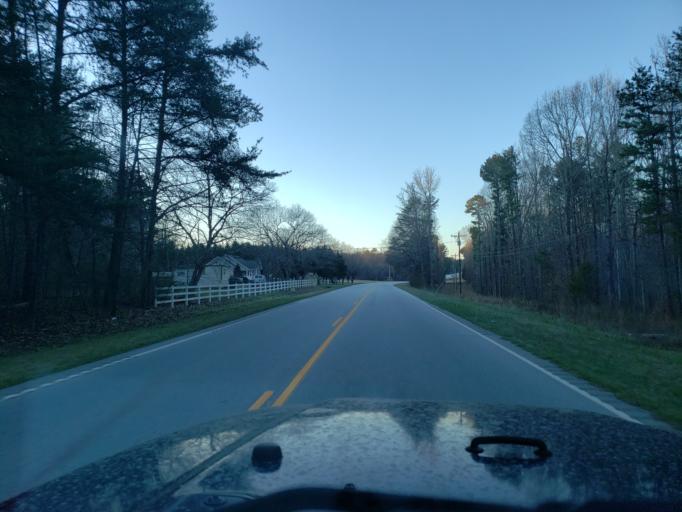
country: US
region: North Carolina
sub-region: Cleveland County
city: Kings Mountain
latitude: 35.1555
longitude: -81.3246
